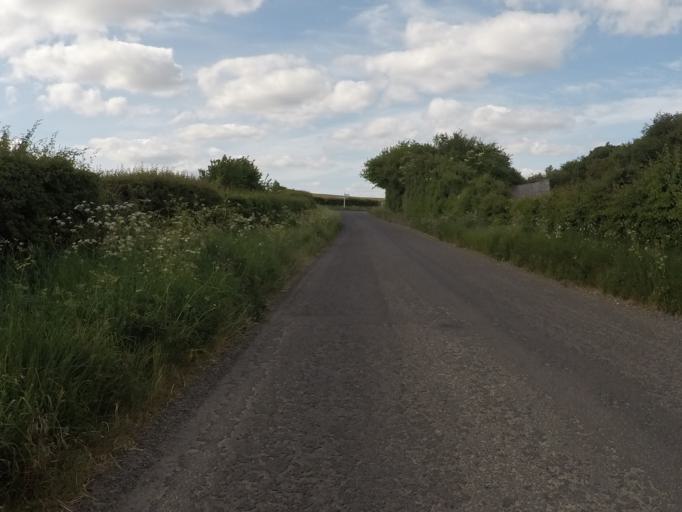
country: GB
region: England
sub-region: Oxfordshire
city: Witney
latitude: 51.8191
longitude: -1.5252
